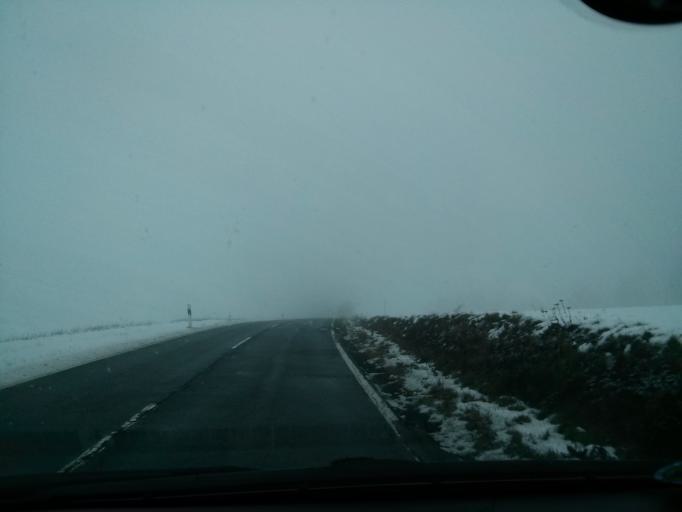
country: DE
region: Rheinland-Pfalz
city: Berg
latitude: 50.5692
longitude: 6.9522
